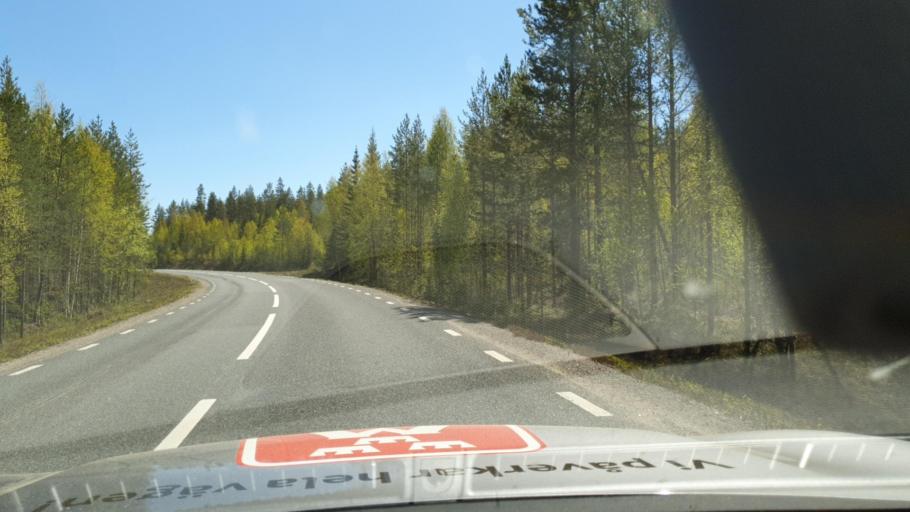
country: SE
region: Vaesternorrland
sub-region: OErnskoeldsviks Kommun
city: Bredbyn
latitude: 63.8182
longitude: 18.4814
